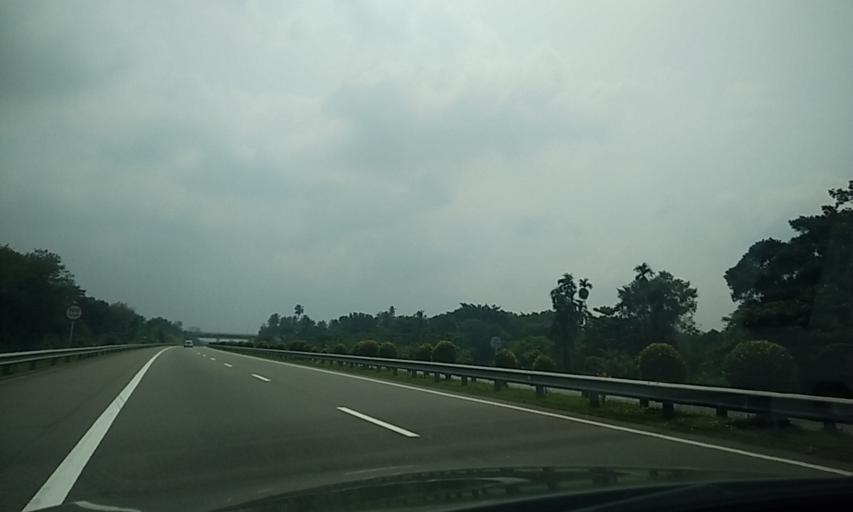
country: LK
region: Western
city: Homagama
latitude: 6.8680
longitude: 79.9786
